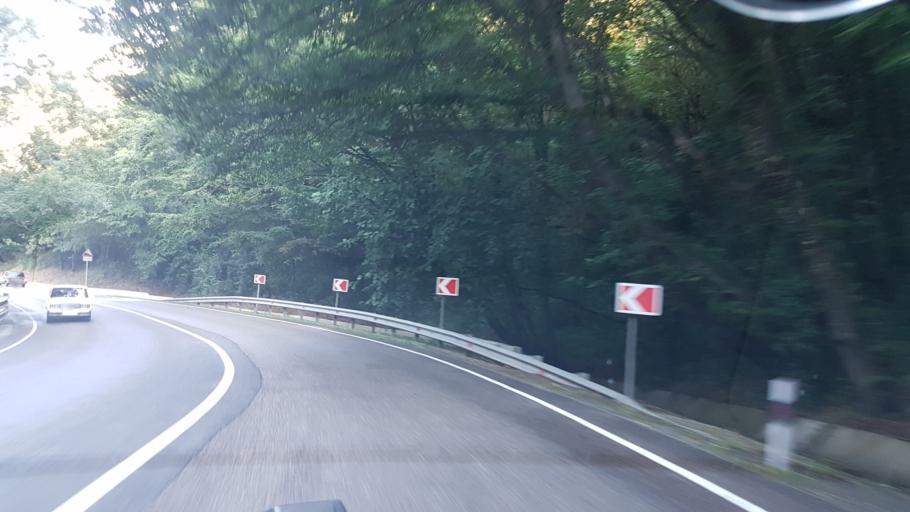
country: RU
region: Krasnodarskiy
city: Gornoye Loo
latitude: 43.6765
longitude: 39.6110
